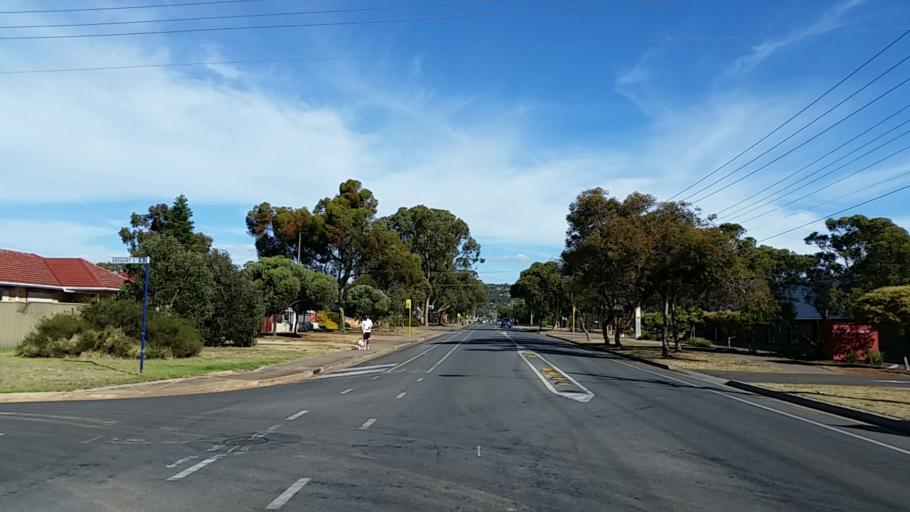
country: AU
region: South Australia
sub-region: Salisbury
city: Salisbury
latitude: -34.7803
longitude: 138.6495
